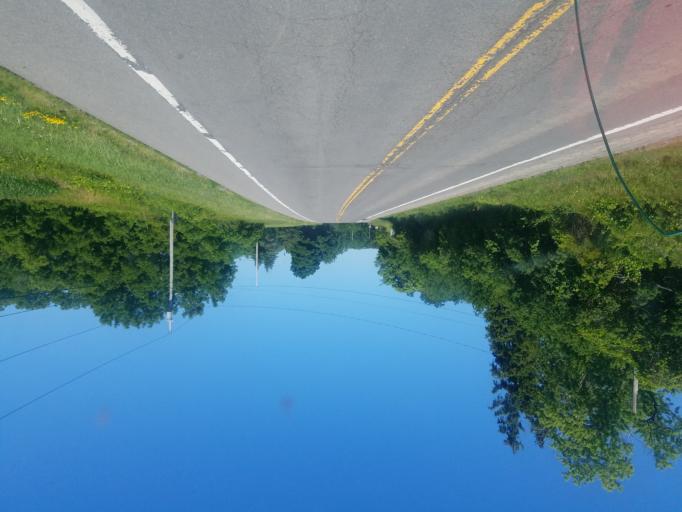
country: US
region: New York
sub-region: Ontario County
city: Geneva
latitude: 42.8451
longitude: -77.0243
